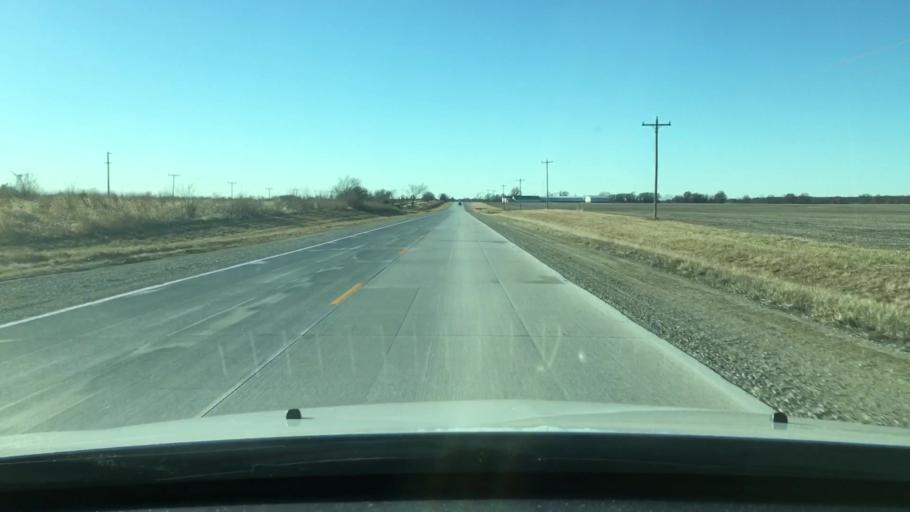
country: US
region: Missouri
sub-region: Boone County
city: Centralia
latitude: 39.2001
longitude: -92.0534
